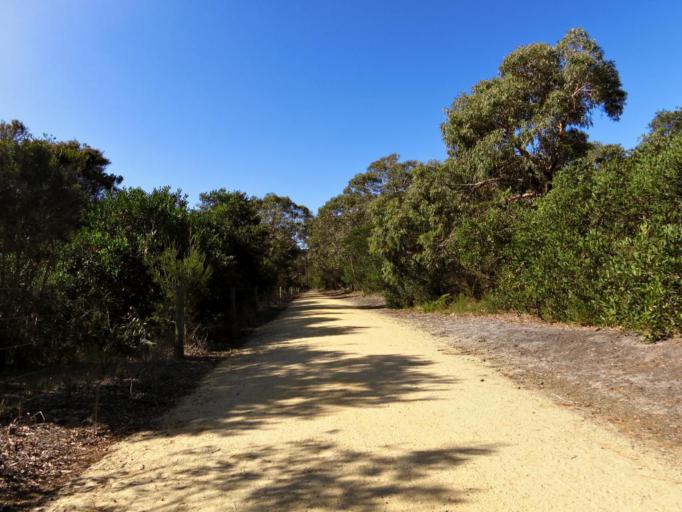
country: AU
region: Victoria
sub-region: Bass Coast
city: North Wonthaggi
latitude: -38.5977
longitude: 145.5683
